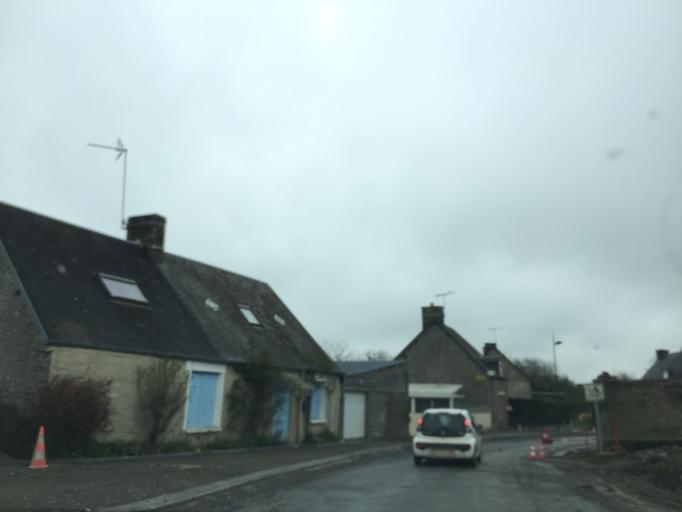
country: FR
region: Lower Normandy
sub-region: Departement de la Manche
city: Pontorson
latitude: 48.5783
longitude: -1.4531
